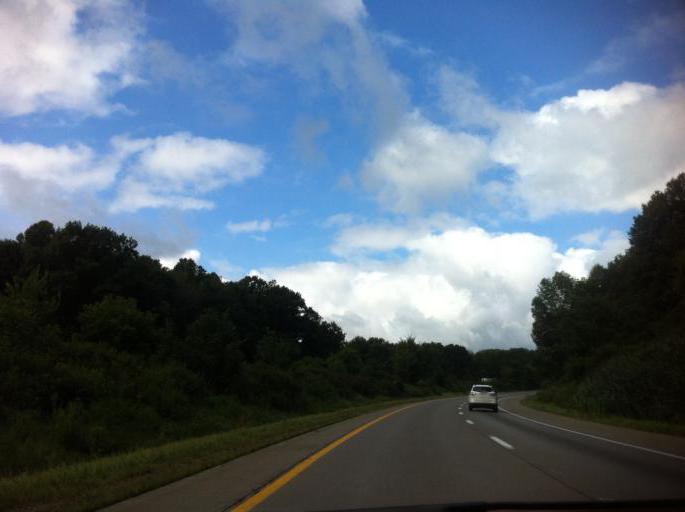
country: US
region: Pennsylvania
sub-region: Mercer County
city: Mercer
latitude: 41.1856
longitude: -80.2636
